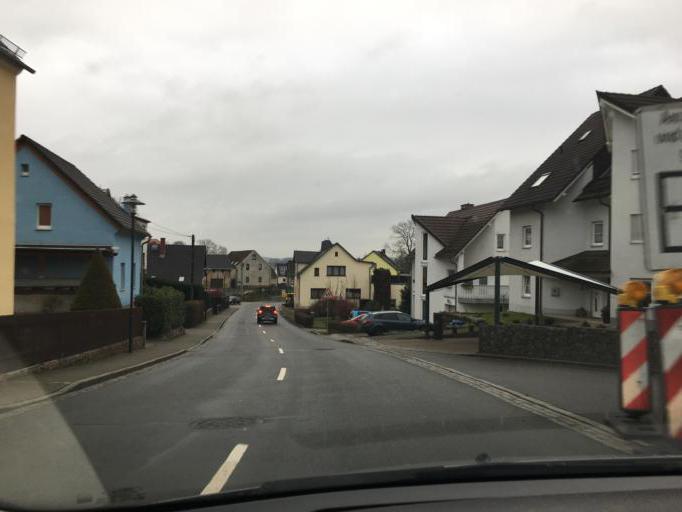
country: DE
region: Saxony
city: Pfaffroda
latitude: 50.8485
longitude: 12.5349
